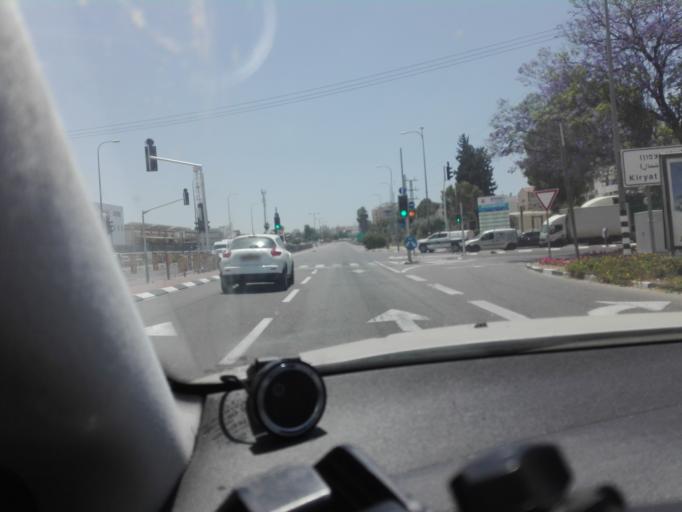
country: IL
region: Central District
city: Bene 'Ayish
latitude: 31.7307
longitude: 34.7539
